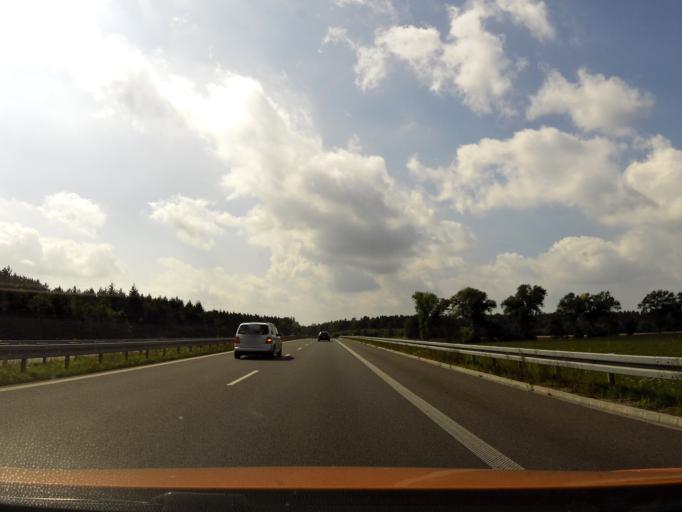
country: PL
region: West Pomeranian Voivodeship
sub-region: Powiat goleniowski
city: Nowogard
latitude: 53.6736
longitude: 15.0803
